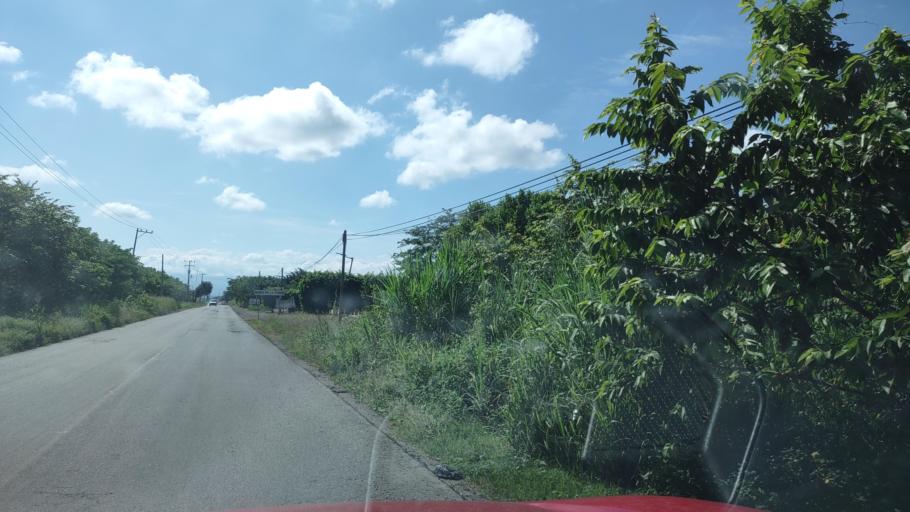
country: MX
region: Veracruz
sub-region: Martinez de la Torre
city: La Union Paso Largo
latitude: 20.1344
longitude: -96.9974
